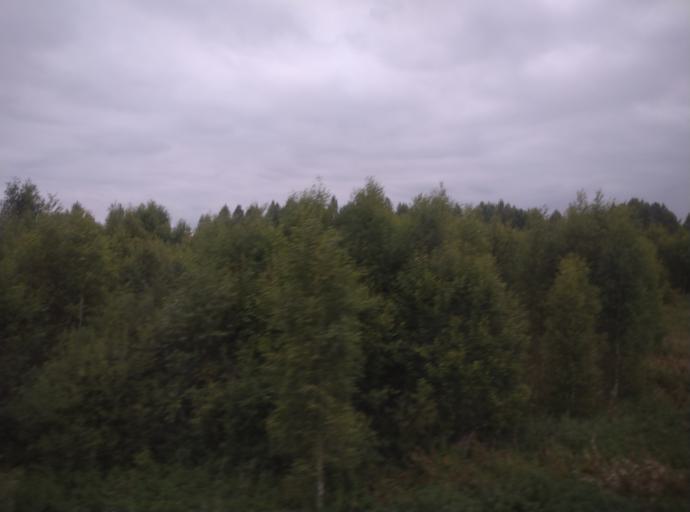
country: RU
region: Kostroma
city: Kosmynino
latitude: 57.5789
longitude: 40.7469
